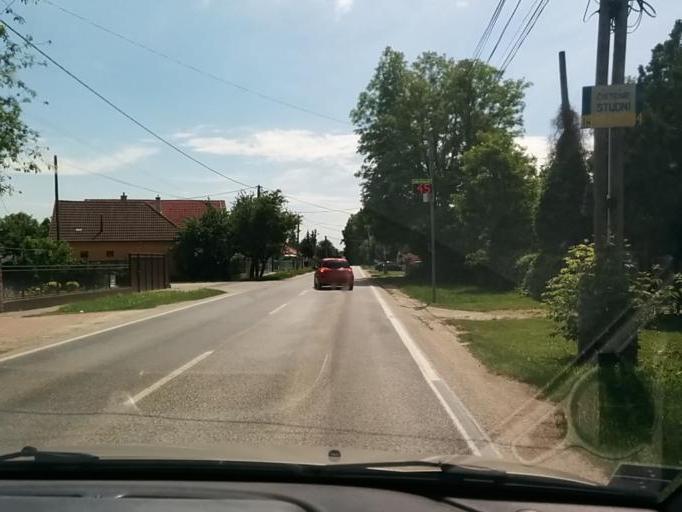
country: SK
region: Trnavsky
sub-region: Okres Galanta
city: Galanta
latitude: 48.2611
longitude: 17.8059
